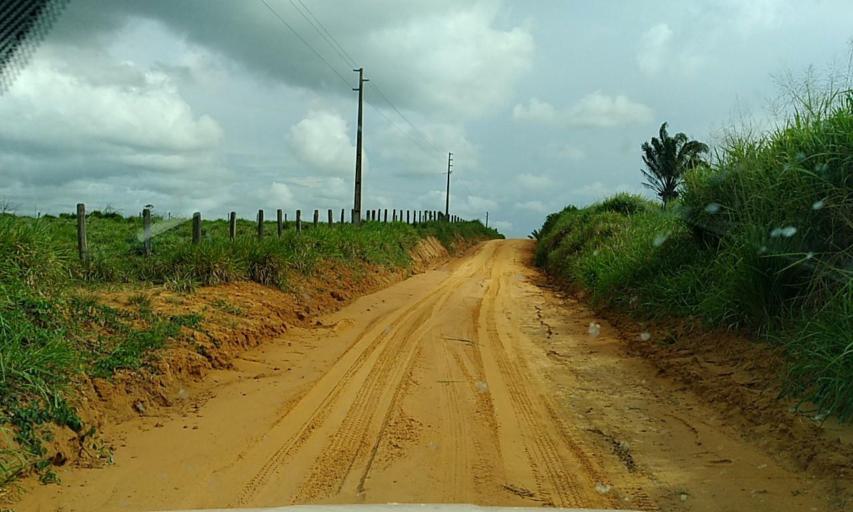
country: BR
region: Para
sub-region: Altamira
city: Altamira
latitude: -3.2262
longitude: -52.6959
